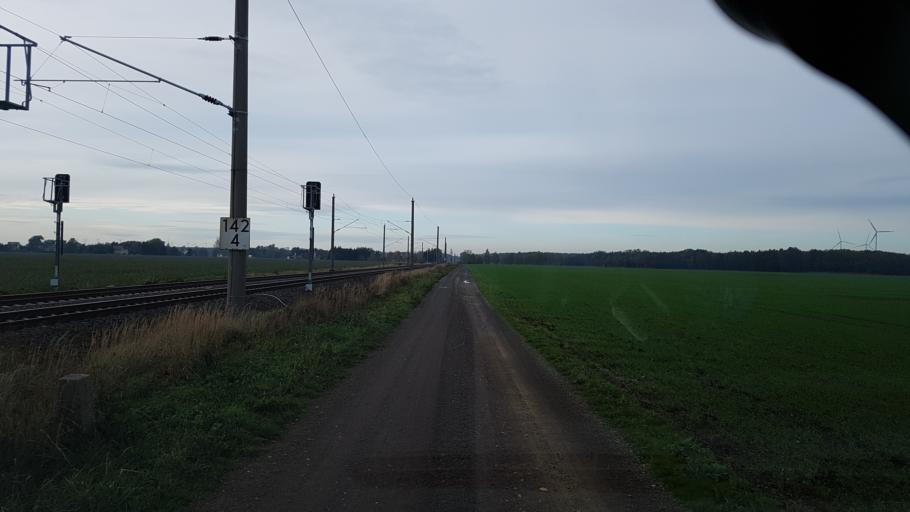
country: DE
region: Brandenburg
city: Falkenberg
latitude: 51.5519
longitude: 13.3063
